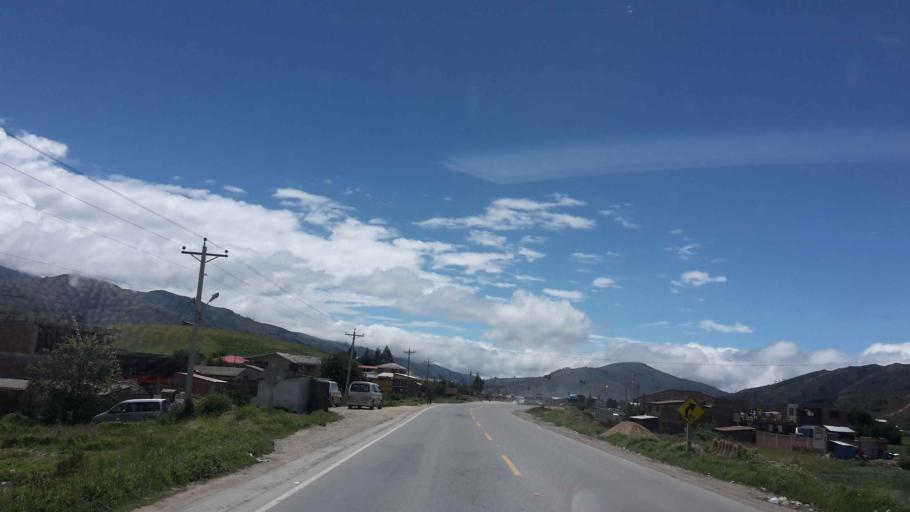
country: BO
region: Cochabamba
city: Colomi
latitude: -17.3294
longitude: -65.8729
